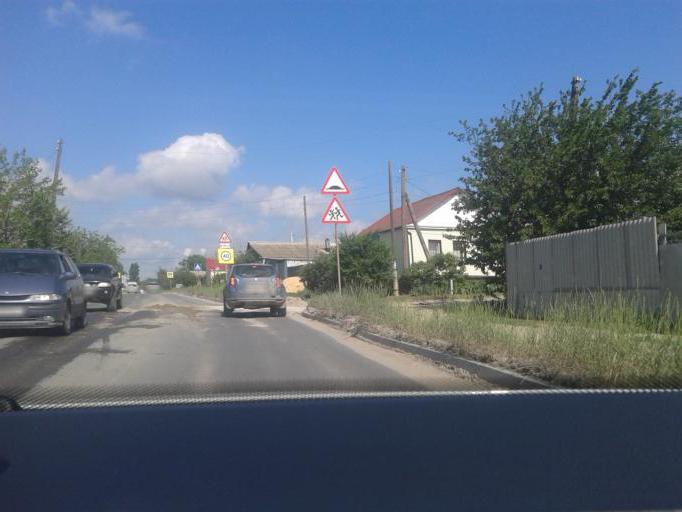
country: RU
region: Volgograd
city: Volgograd
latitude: 48.6934
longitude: 44.4530
